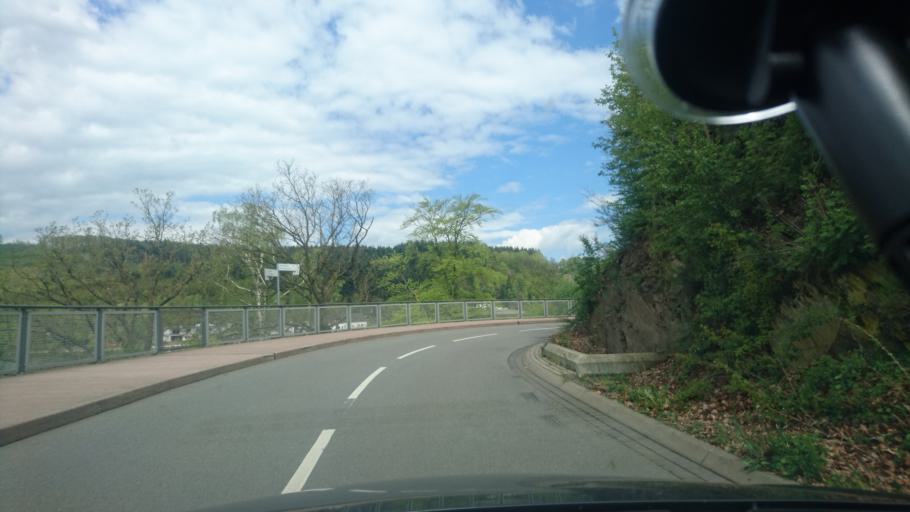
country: DE
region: Hesse
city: Willingen
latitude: 51.3716
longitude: 8.7260
